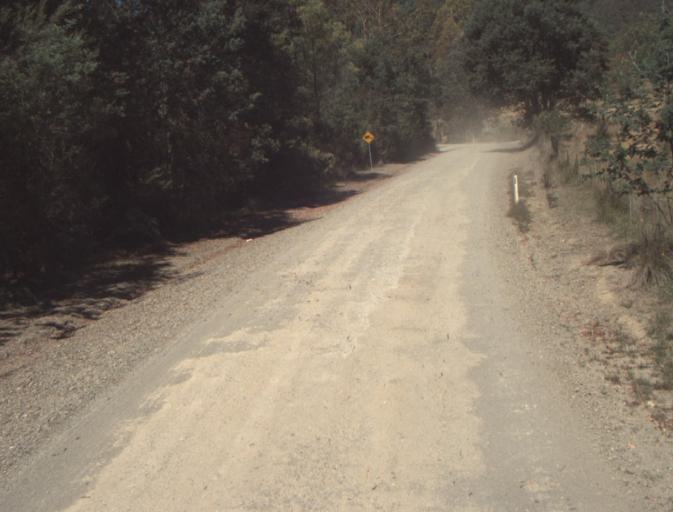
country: AU
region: Tasmania
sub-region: Dorset
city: Scottsdale
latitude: -41.2925
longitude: 147.3933
